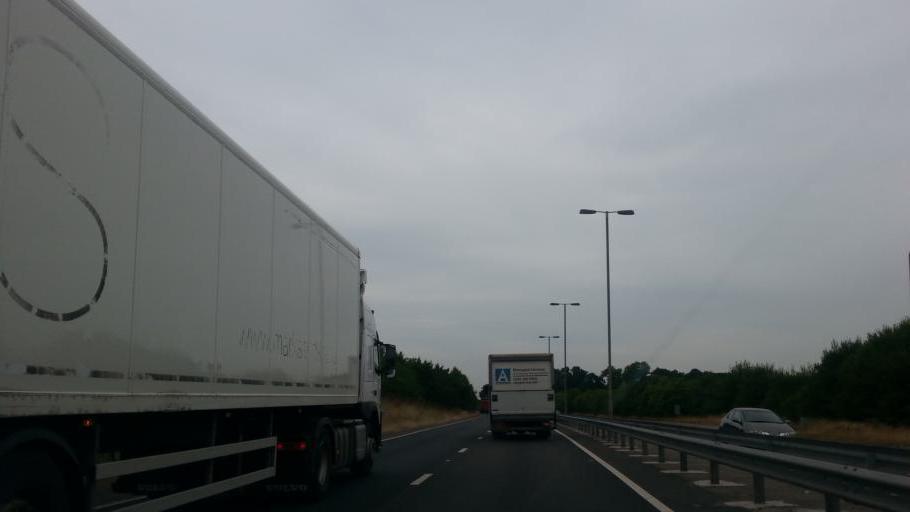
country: GB
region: England
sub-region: Derbyshire
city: Borrowash
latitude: 52.8857
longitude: -1.4045
